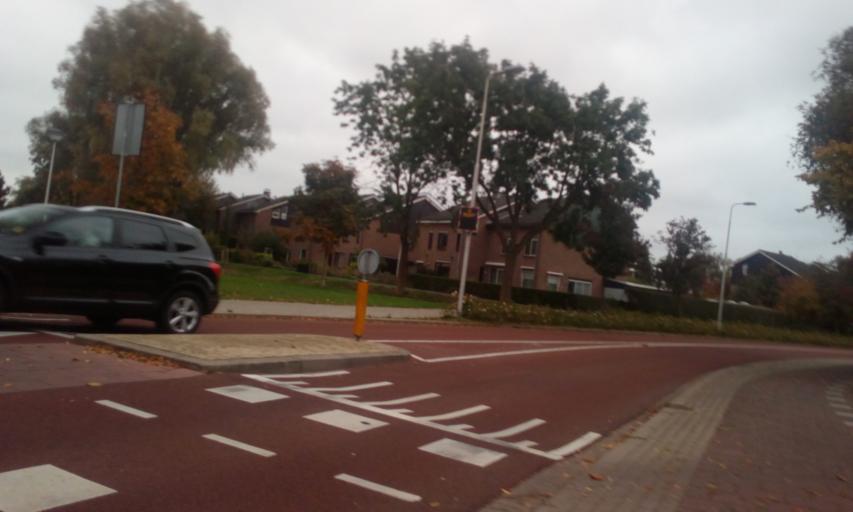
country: NL
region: South Holland
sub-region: Gemeente Lansingerland
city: Bergschenhoek
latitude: 52.0028
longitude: 4.4914
